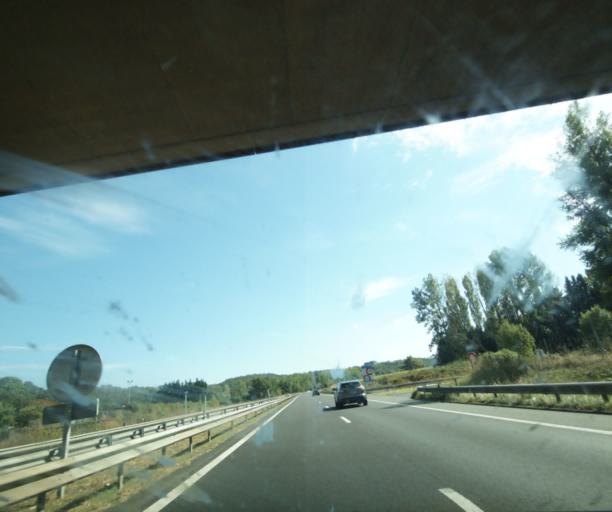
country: FR
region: Limousin
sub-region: Departement de la Correze
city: Saint-Pantaleon-de-Larche
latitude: 45.1404
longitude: 1.4882
